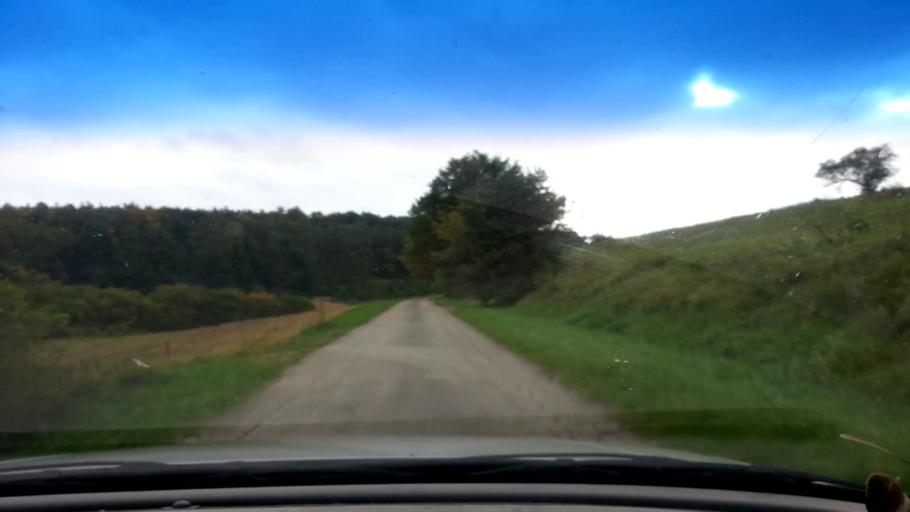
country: DE
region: Bavaria
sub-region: Upper Franconia
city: Priesendorf
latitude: 49.8938
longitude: 10.7072
